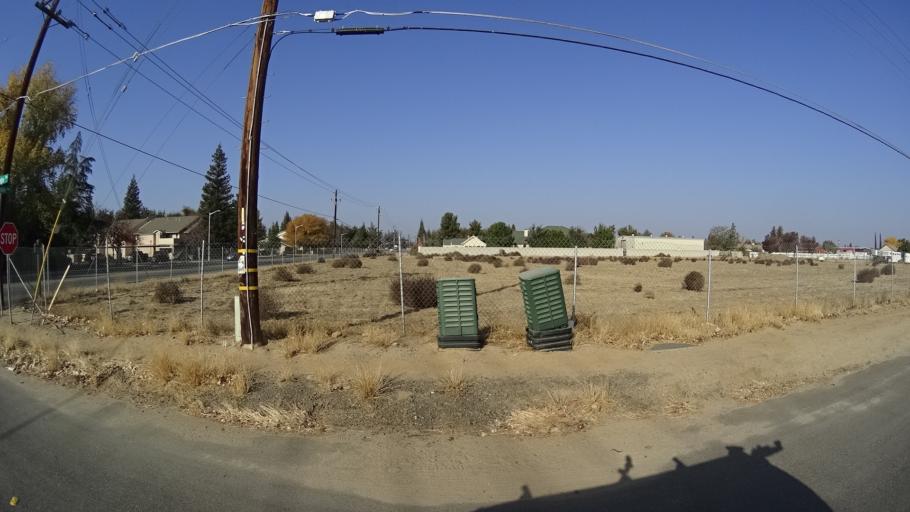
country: US
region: California
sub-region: Kern County
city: Greenacres
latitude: 35.3978
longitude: -119.0741
